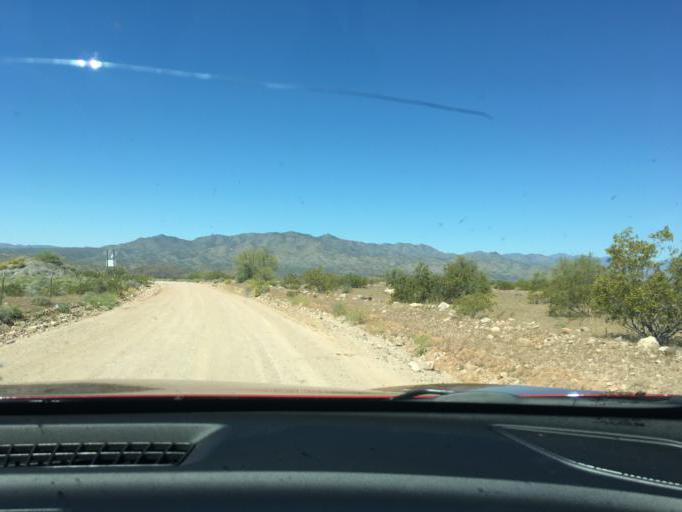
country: US
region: Arizona
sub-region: Yavapai County
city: Bagdad
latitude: 34.6114
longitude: -113.5196
